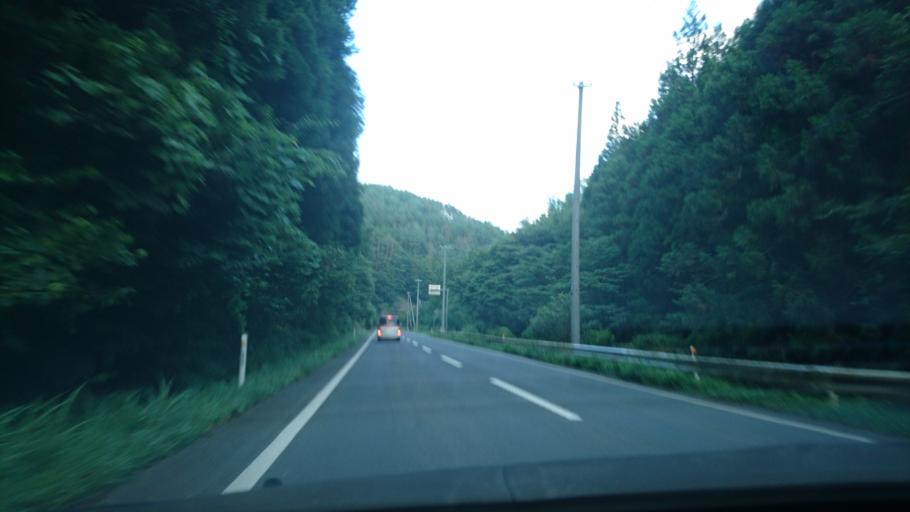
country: JP
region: Iwate
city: Mizusawa
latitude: 39.0426
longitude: 141.2394
